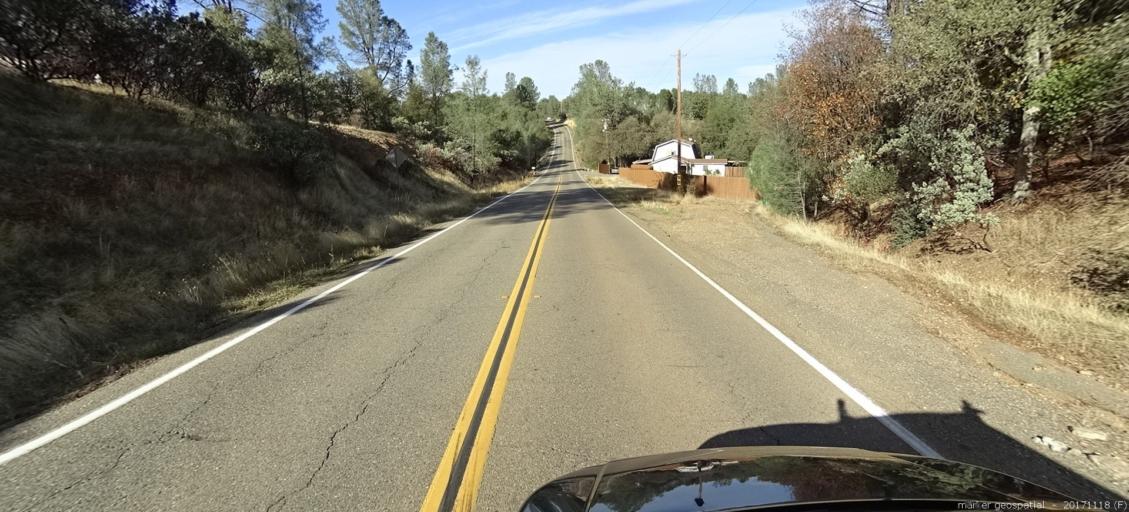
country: US
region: California
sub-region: Shasta County
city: Anderson
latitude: 40.4658
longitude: -122.3969
